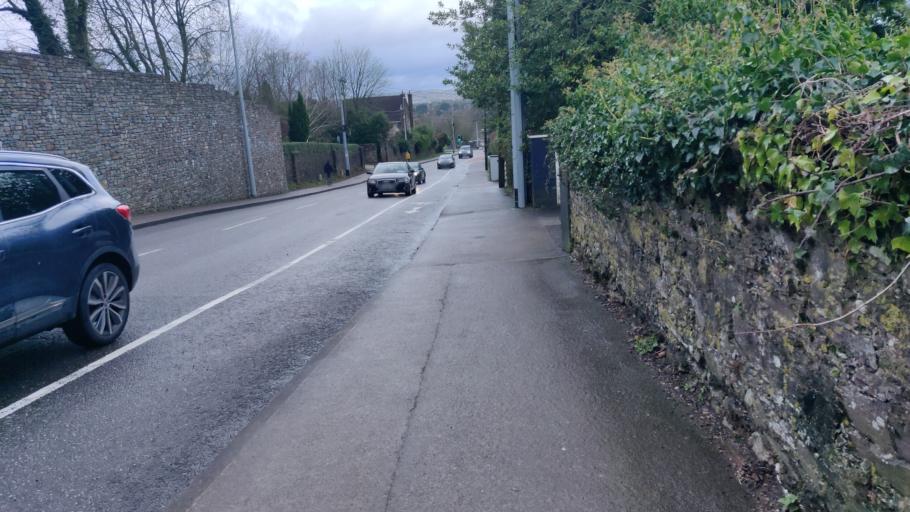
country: IE
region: Munster
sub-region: County Cork
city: Cork
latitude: 51.8735
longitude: -8.4237
